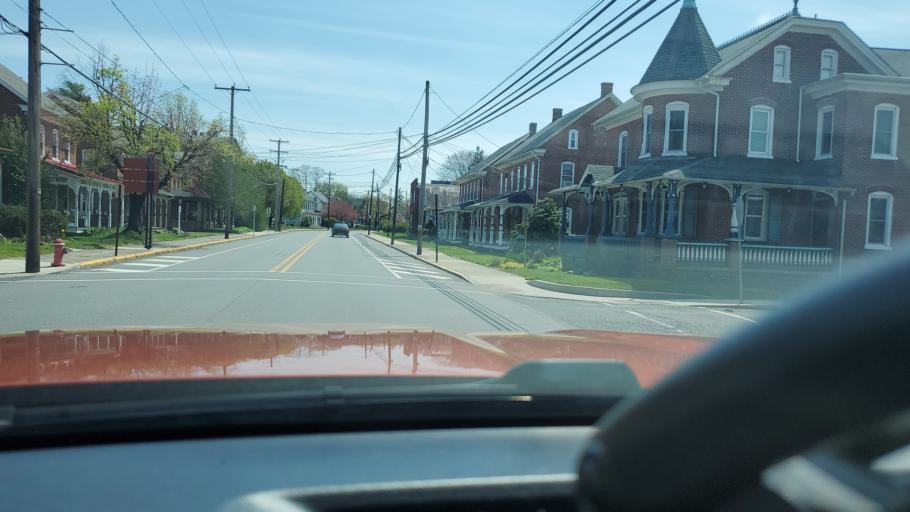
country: US
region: Pennsylvania
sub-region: Montgomery County
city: Red Hill
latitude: 40.3748
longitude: -75.4820
